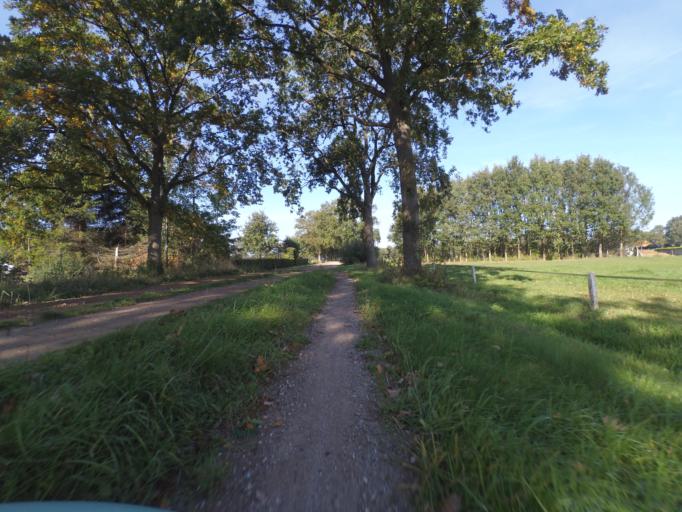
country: NL
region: Gelderland
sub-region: Gemeente Lochem
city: Barchem
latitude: 52.1127
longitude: 6.4049
